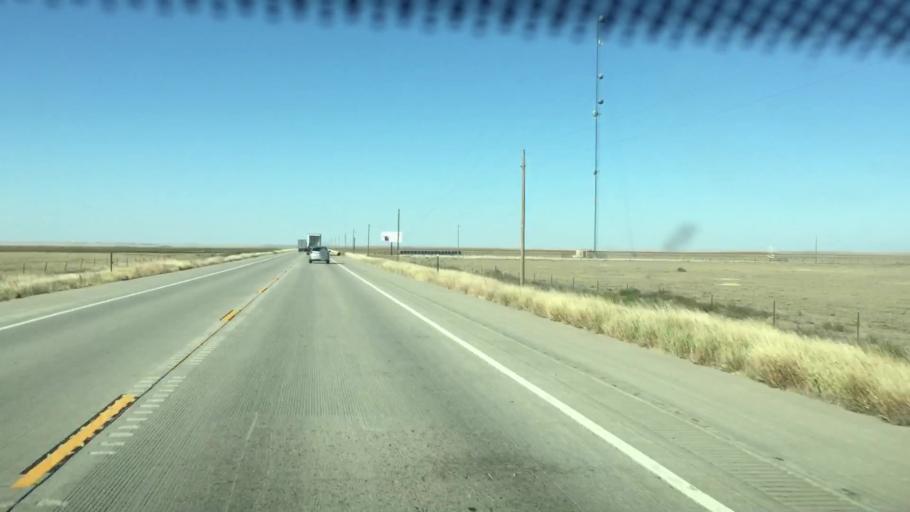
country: US
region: Colorado
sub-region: Kiowa County
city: Eads
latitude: 38.2797
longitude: -102.7199
